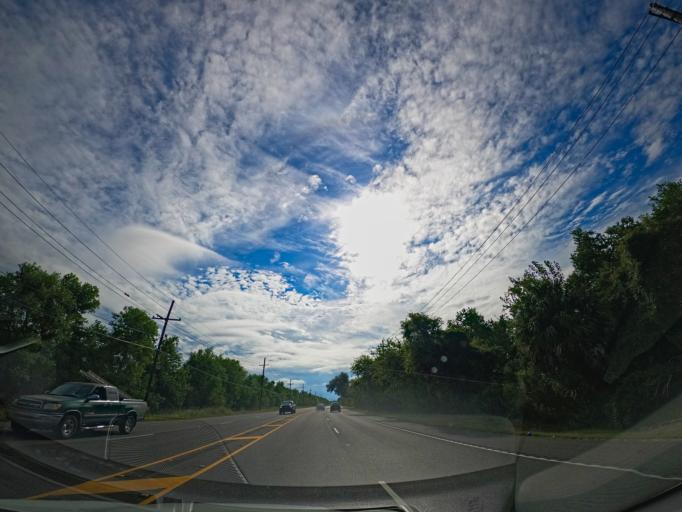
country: US
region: Louisiana
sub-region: Saint Bernard Parish
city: Meraux
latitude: 30.0605
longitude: -89.8678
